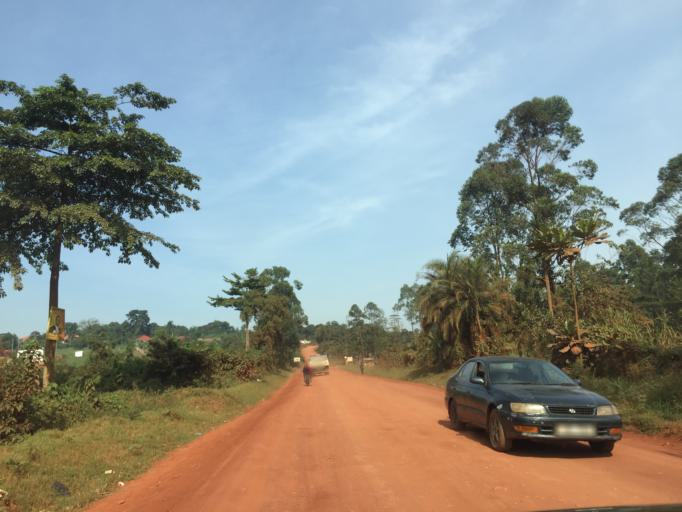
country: UG
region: Central Region
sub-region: Wakiso District
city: Kireka
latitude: 0.4410
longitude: 32.5924
